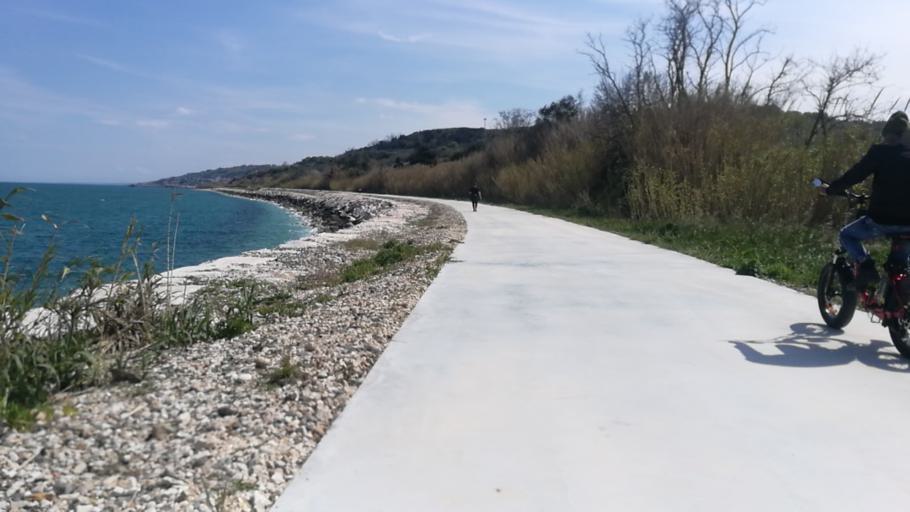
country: IT
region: Abruzzo
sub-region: Provincia di Chieti
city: Marina di San Vito
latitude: 42.3269
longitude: 14.4249
